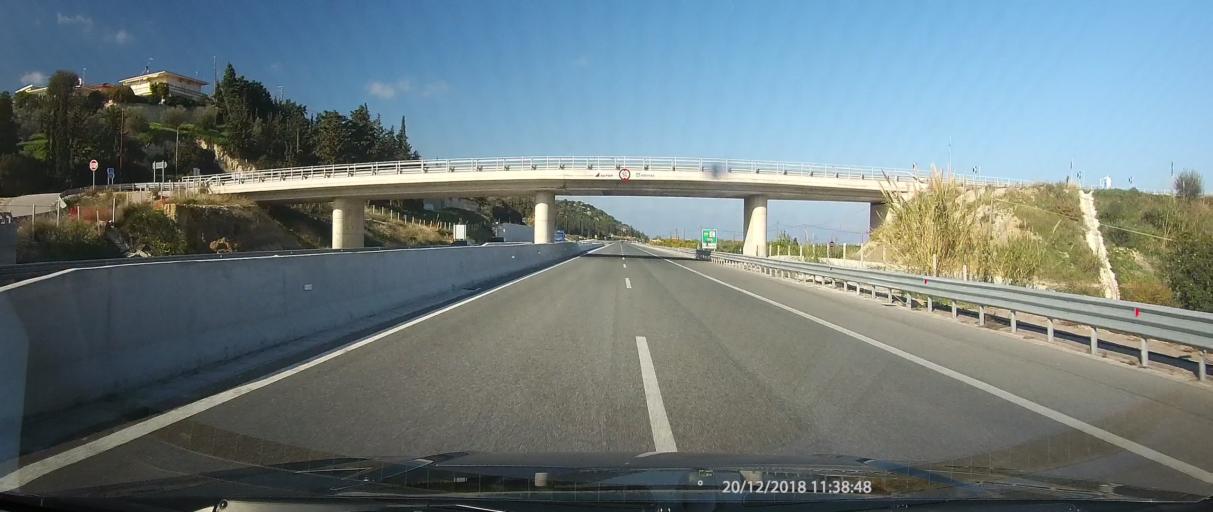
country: GR
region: Peloponnese
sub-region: Nomos Korinthias
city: Kato Dhiminio
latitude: 38.0328
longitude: 22.7172
